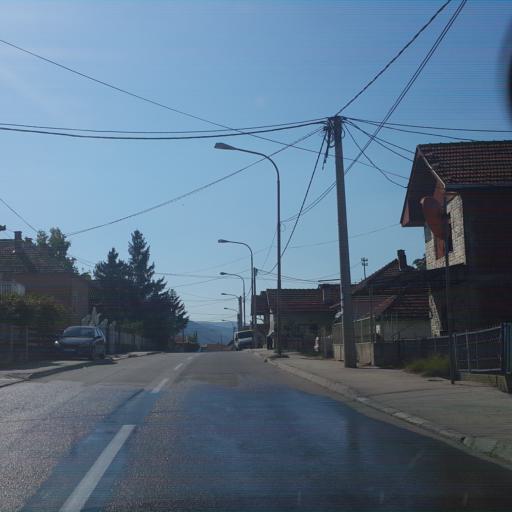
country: RS
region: Central Serbia
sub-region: Zajecarski Okrug
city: Knjazevac
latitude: 43.5582
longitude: 22.2523
